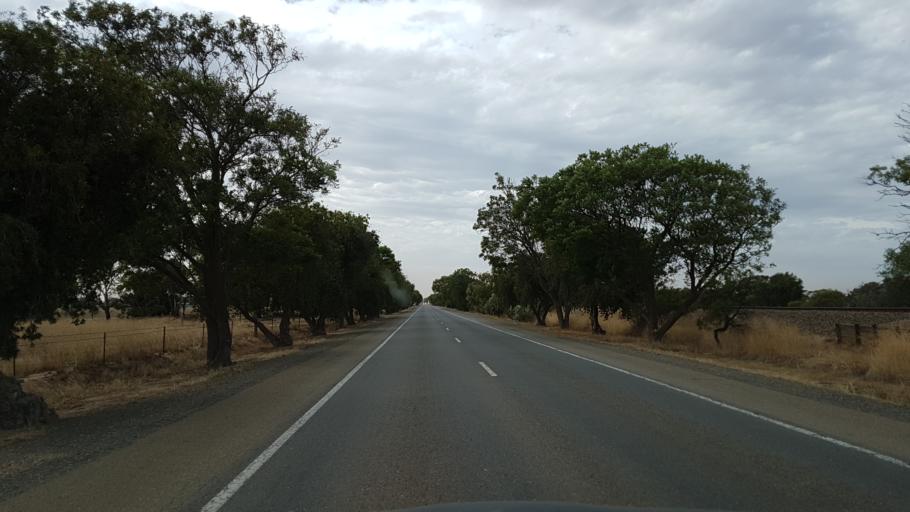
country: AU
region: South Australia
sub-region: Mallala
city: Mallala
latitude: -34.4331
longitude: 138.4999
